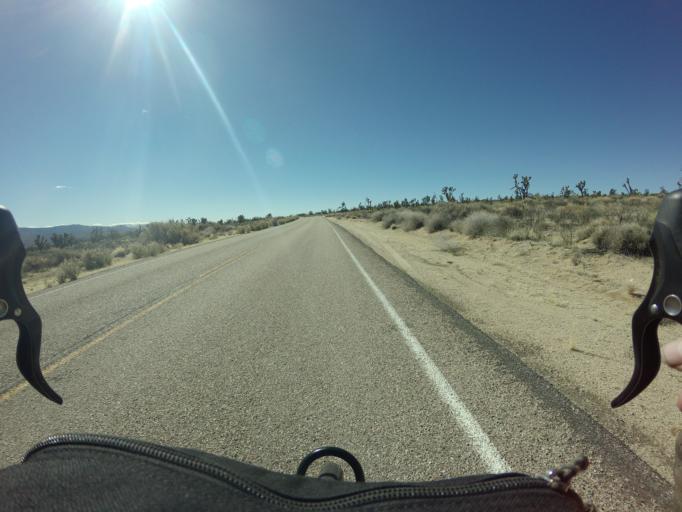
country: US
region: Nevada
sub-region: Clark County
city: Sandy Valley
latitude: 35.2869
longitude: -115.4966
